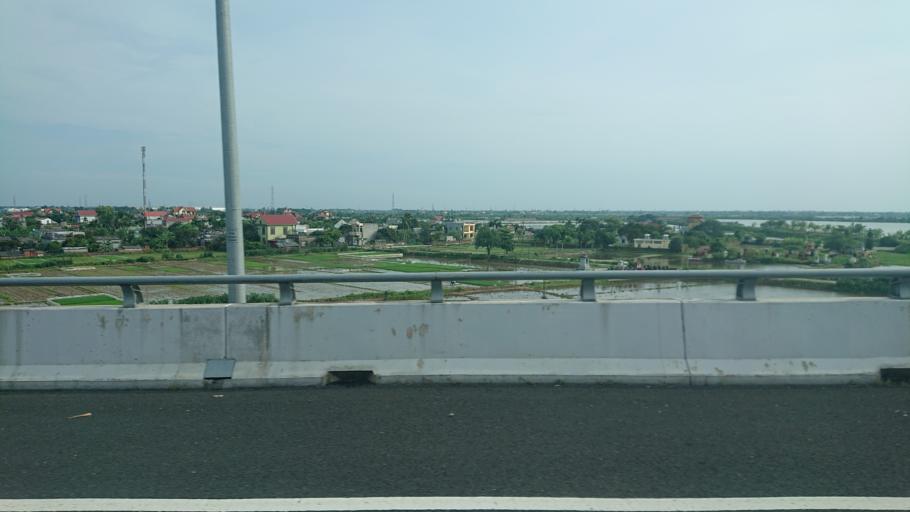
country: VN
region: Hai Phong
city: An Lao
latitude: 20.8067
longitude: 106.5156
